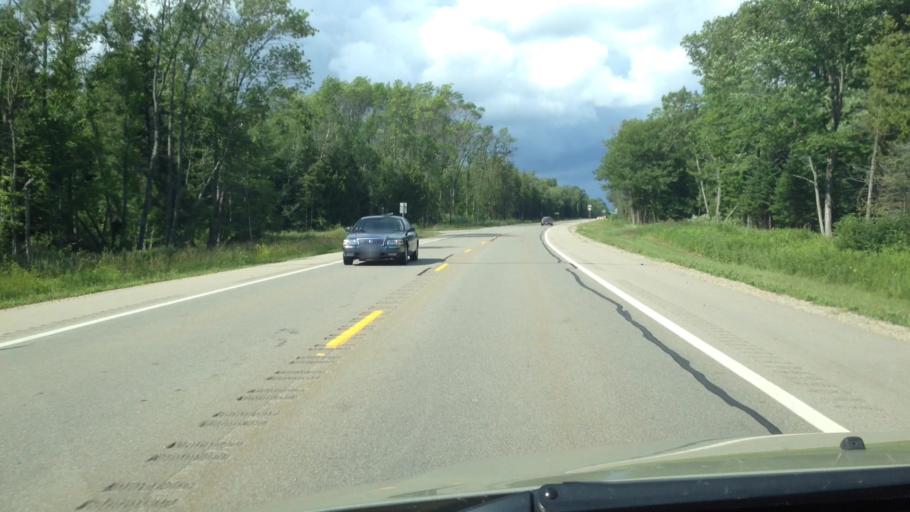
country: US
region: Michigan
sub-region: Menominee County
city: Menominee
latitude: 45.3080
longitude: -87.4387
